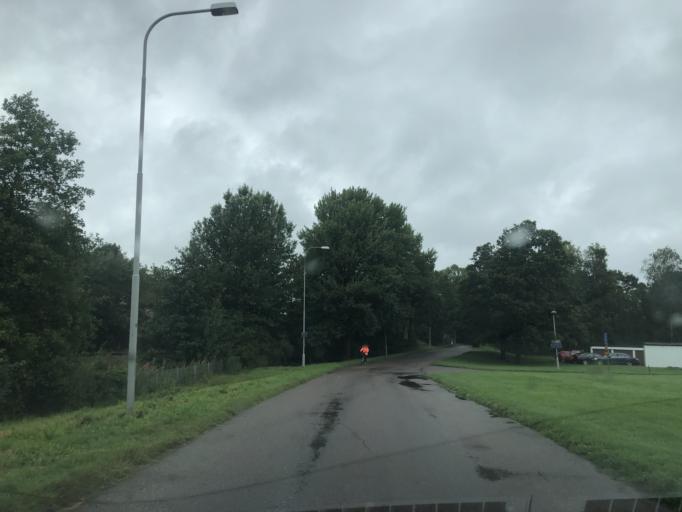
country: SE
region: Vaestra Goetaland
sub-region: Goteborg
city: Goeteborg
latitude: 57.7638
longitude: 11.9442
